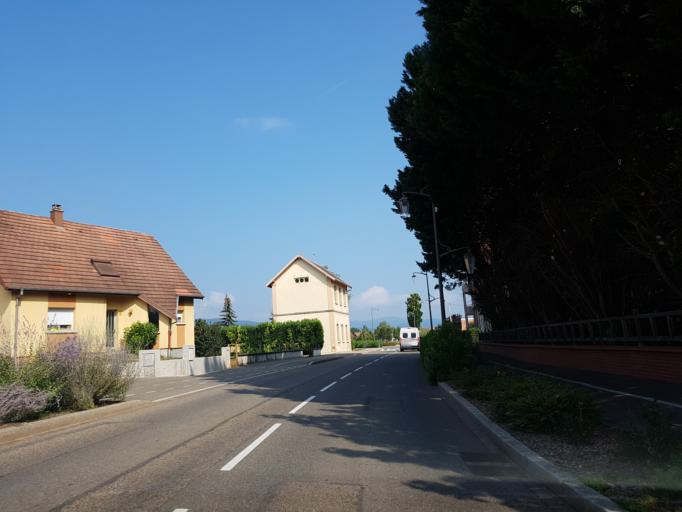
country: FR
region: Alsace
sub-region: Departement du Haut-Rhin
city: Eguisheim
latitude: 48.0449
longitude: 7.3107
